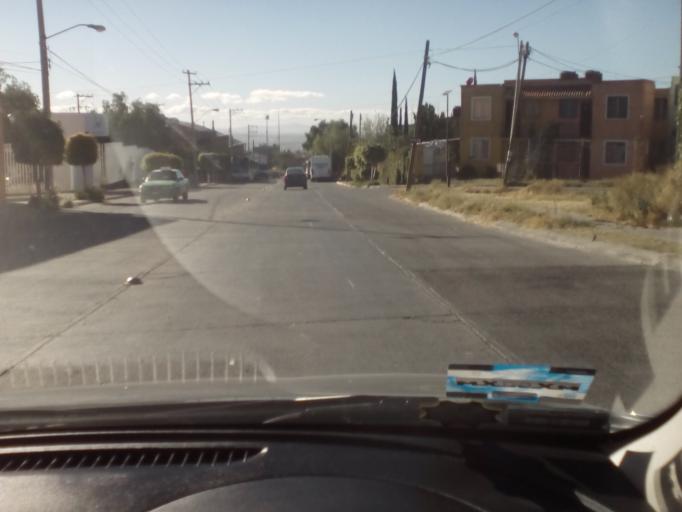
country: MX
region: Guanajuato
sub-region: Leon
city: Ejido la Joya
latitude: 21.1312
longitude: -101.7153
